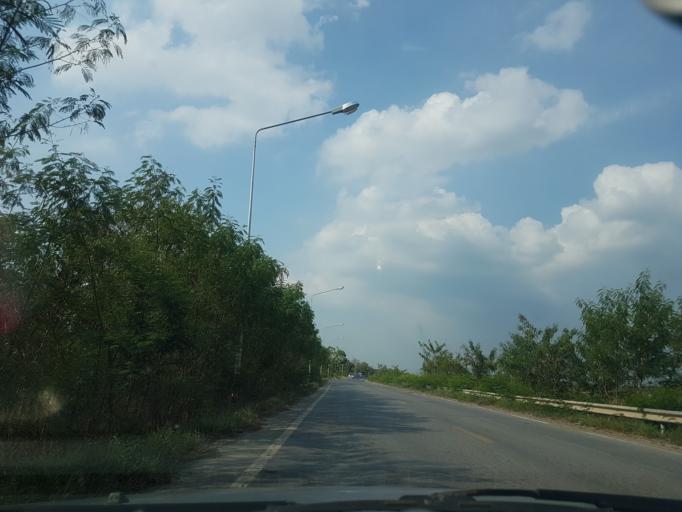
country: TH
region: Phra Nakhon Si Ayutthaya
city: Phachi
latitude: 14.4056
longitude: 100.7871
